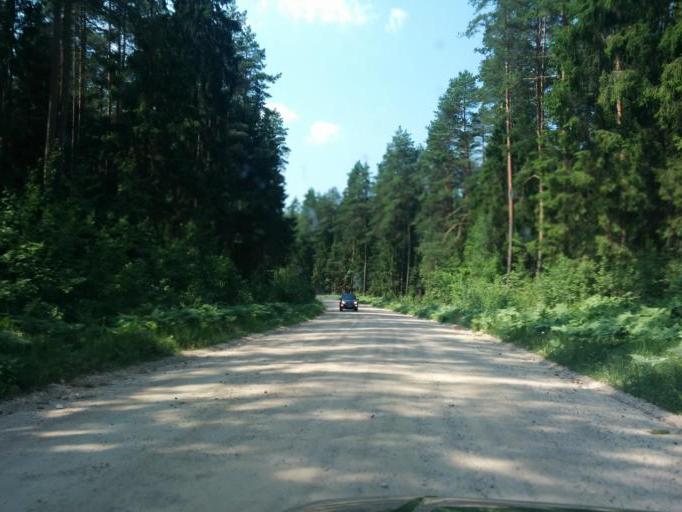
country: LV
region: Baldone
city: Baldone
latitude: 56.7473
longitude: 24.4475
